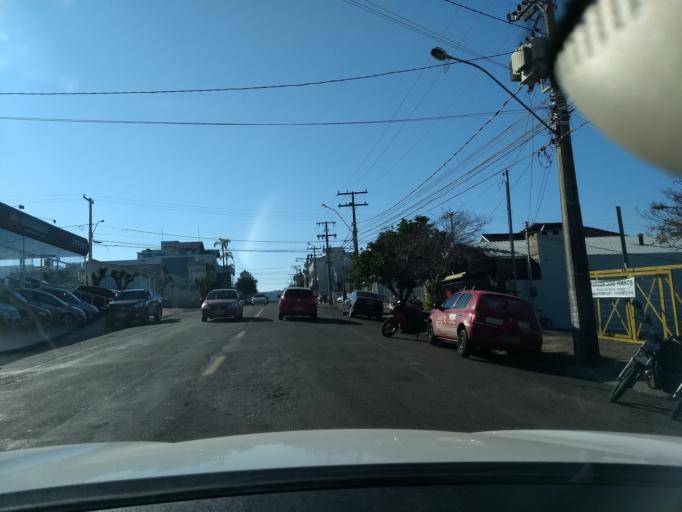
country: BR
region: Rio Grande do Sul
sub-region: Santa Cruz Do Sul
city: Santa Cruz do Sul
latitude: -29.7161
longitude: -52.4411
